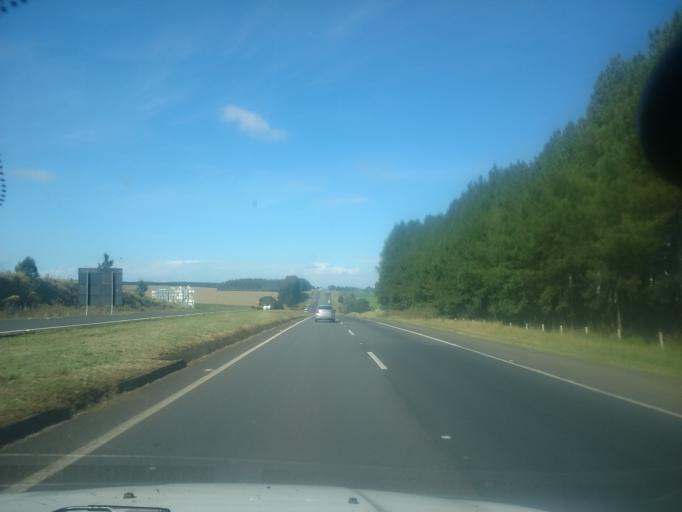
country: BR
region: Parana
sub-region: Palmeira
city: Palmeira
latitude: -25.3511
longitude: -49.8390
